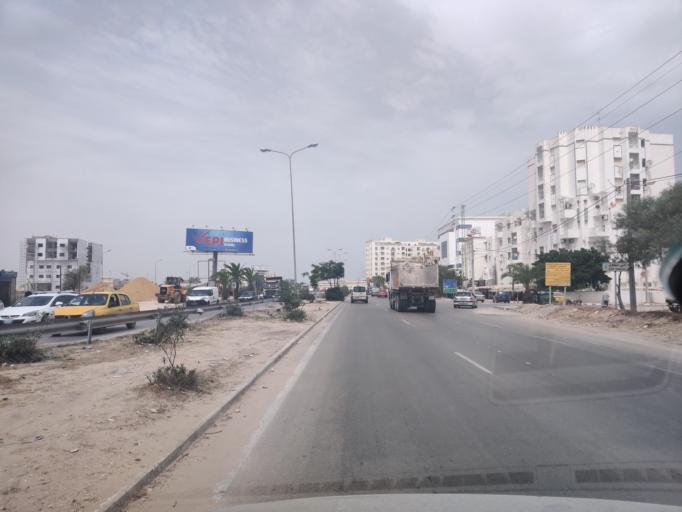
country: TN
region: Susah
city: Hammam Sousse
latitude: 35.8302
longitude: 10.5905
